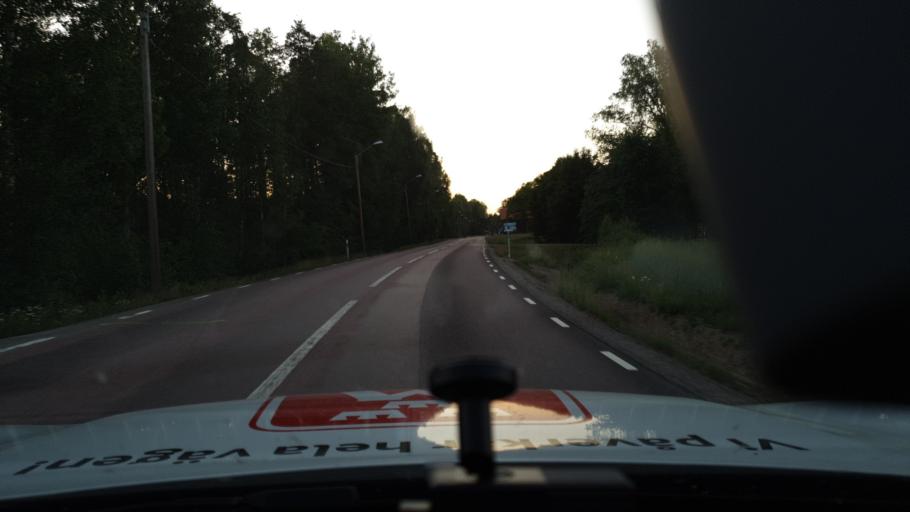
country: SE
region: Vaermland
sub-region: Torsby Kommun
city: Torsby
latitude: 60.2799
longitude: 13.0322
